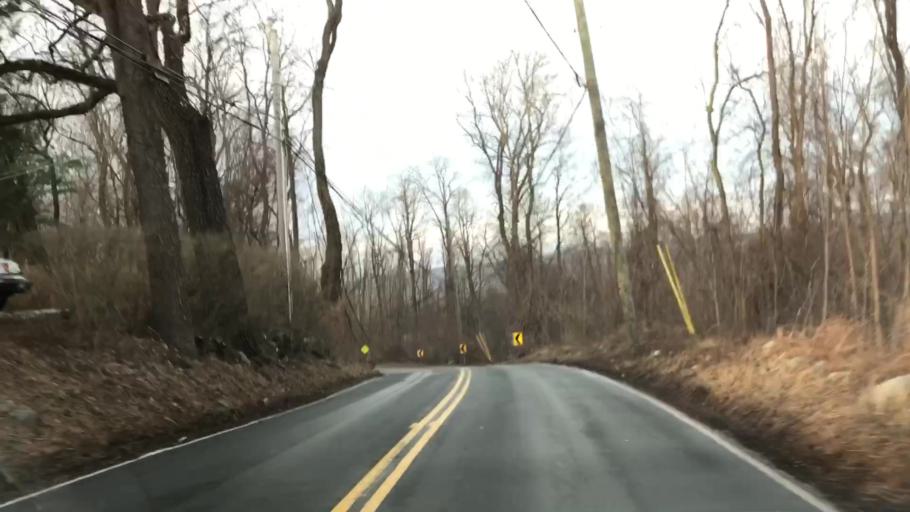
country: US
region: New York
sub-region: Rockland County
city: Viola
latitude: 41.1367
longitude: -74.0872
